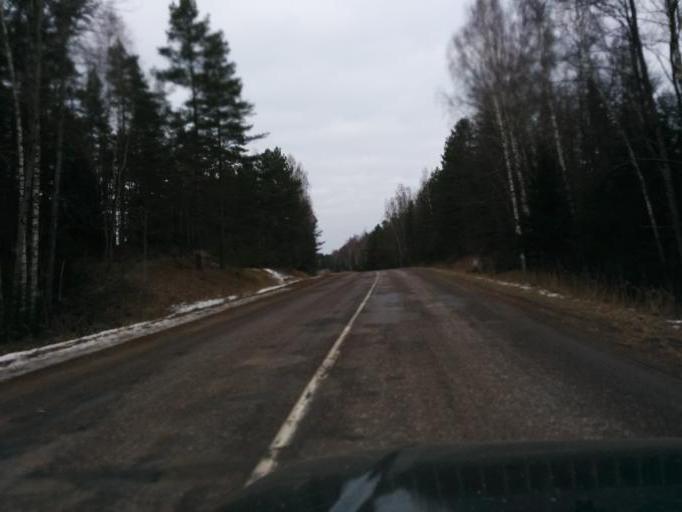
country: LV
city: Tireli
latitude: 56.8737
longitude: 23.5409
